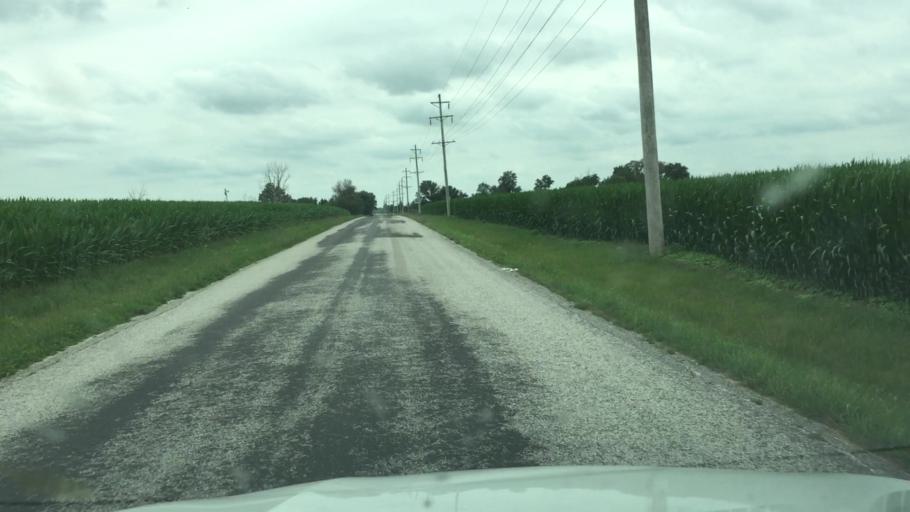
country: US
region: Illinois
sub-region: Hancock County
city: Carthage
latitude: 40.3918
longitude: -91.0827
